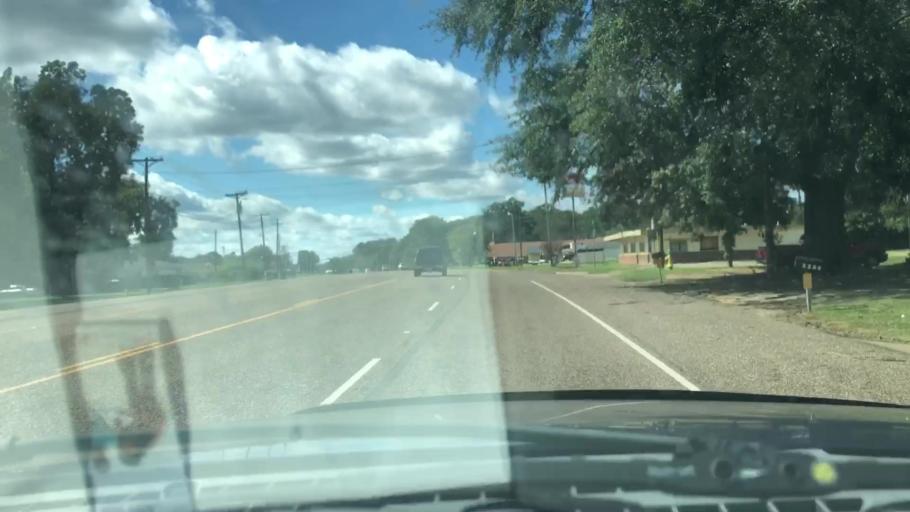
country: US
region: Texas
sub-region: Bowie County
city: Texarkana
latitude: 33.4023
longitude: -94.0766
